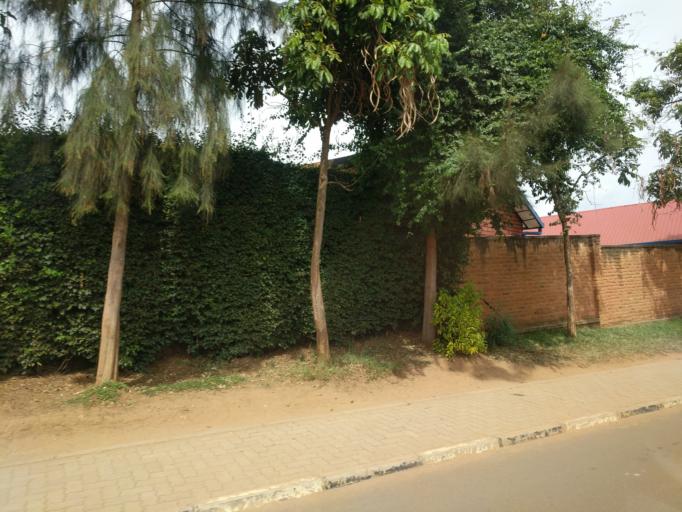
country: RW
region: Kigali
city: Kigali
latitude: -1.9794
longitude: 30.1142
